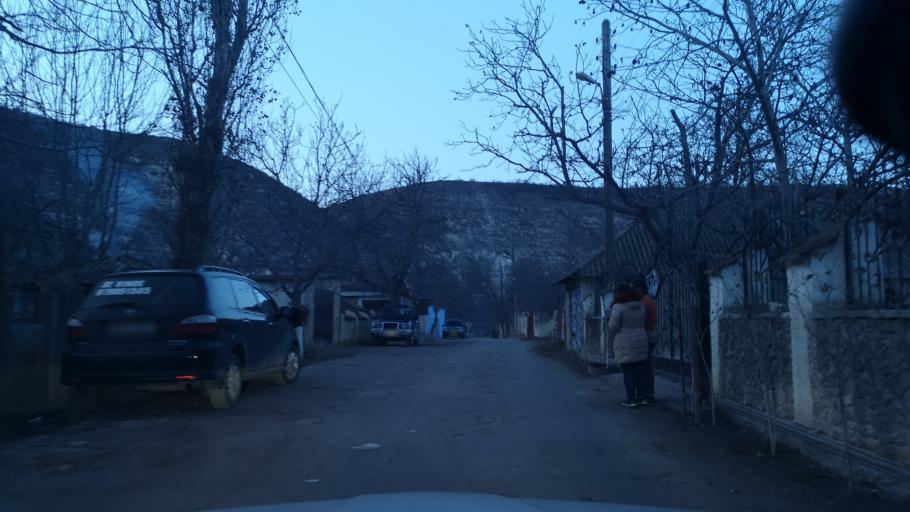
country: MD
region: Telenesti
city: Cocieri
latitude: 47.3047
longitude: 28.9619
